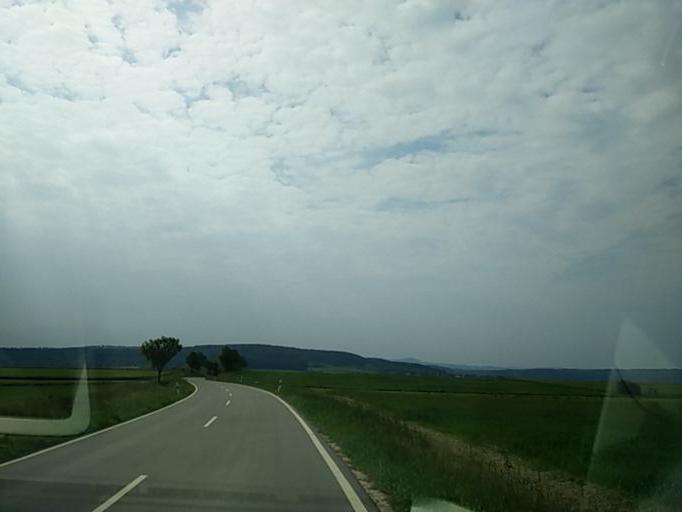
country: DE
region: Baden-Wuerttemberg
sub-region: Tuebingen Region
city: Hirrlingen
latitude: 48.4219
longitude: 8.8821
